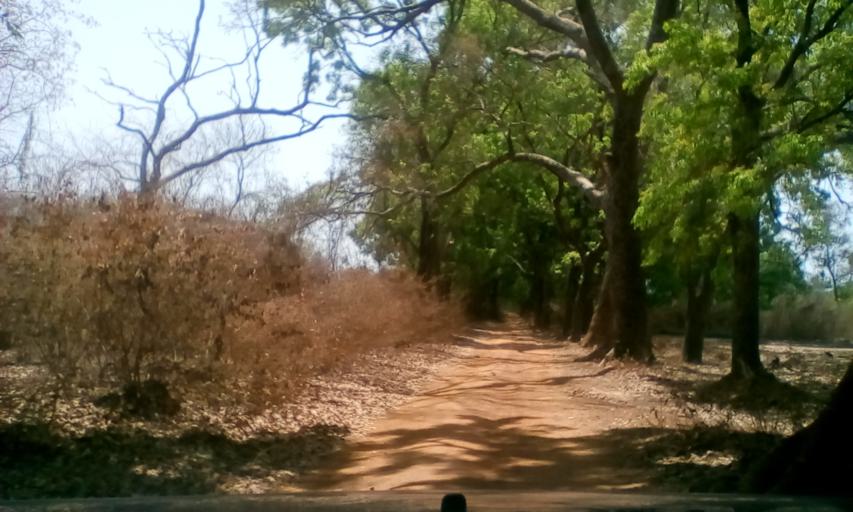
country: GW
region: Oio
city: Farim
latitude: 12.4433
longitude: -15.4329
